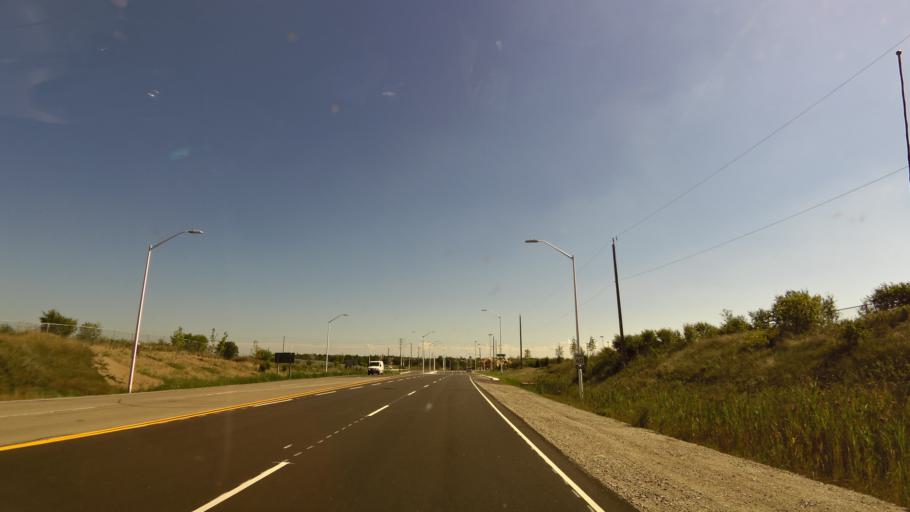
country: CA
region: Ontario
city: Oakville
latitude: 43.4822
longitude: -79.7632
